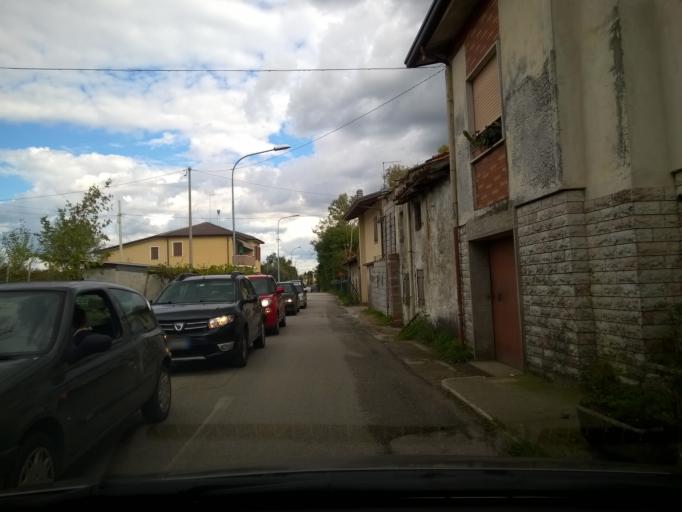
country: IT
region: Veneto
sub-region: Provincia di Treviso
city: Castelfranco Veneto
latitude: 45.6869
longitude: 11.9181
